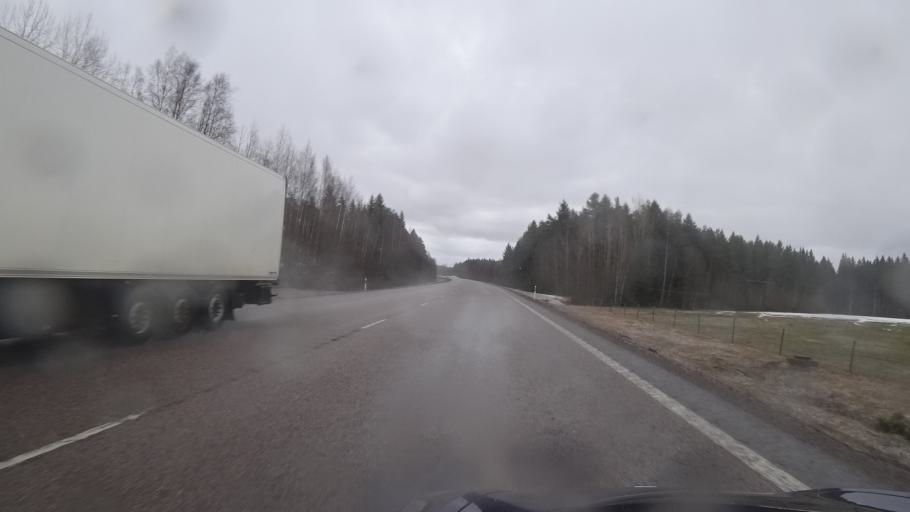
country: FI
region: Paijanne Tavastia
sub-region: Lahti
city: Nastola
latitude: 60.9300
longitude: 25.9308
